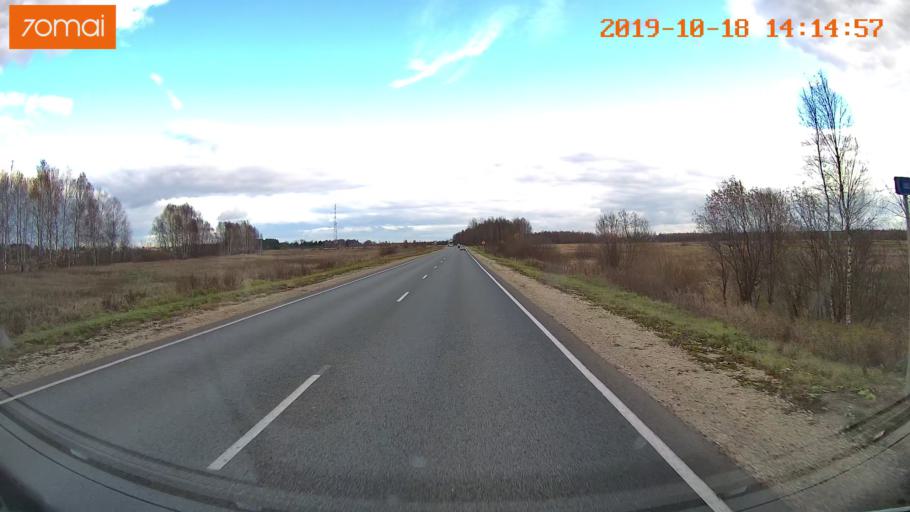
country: RU
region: Rjazan
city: Spas-Klepiki
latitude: 55.1475
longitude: 40.3066
